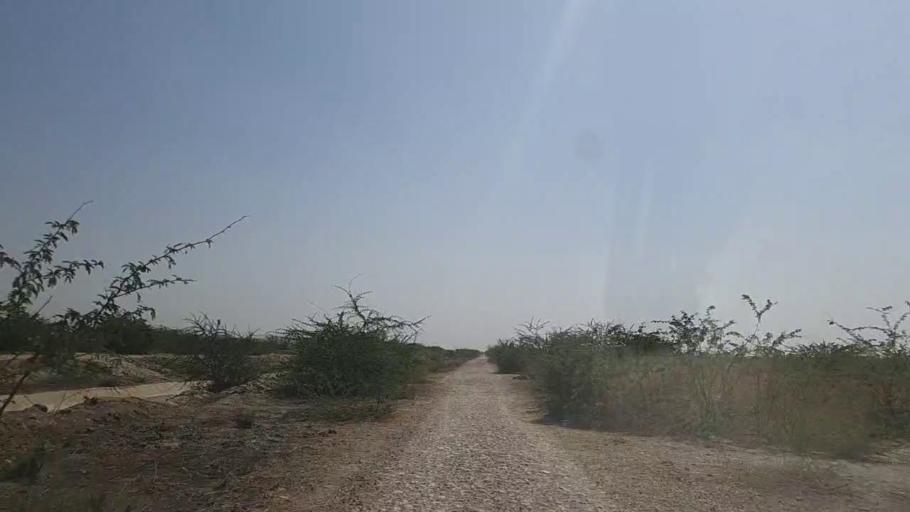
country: PK
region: Sindh
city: Naukot
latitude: 24.6436
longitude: 69.2750
